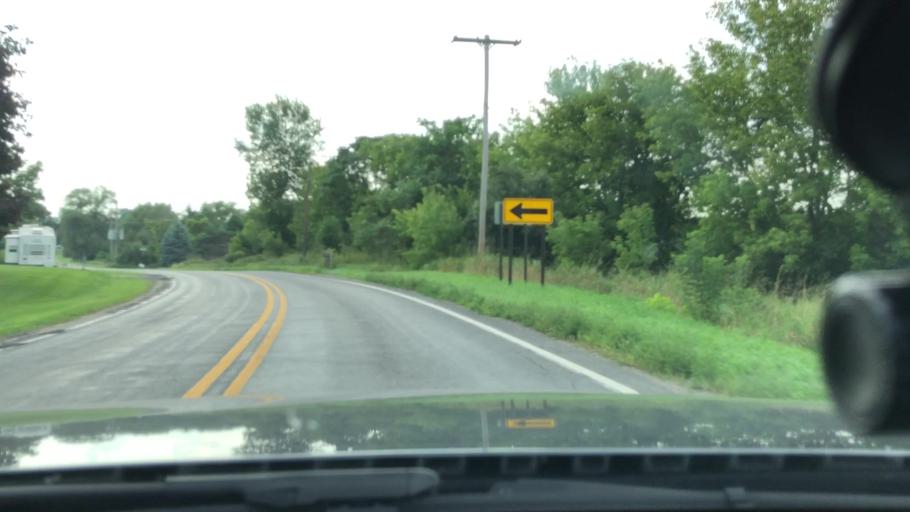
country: US
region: Michigan
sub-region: Washtenaw County
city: Manchester
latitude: 42.1458
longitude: -84.0662
